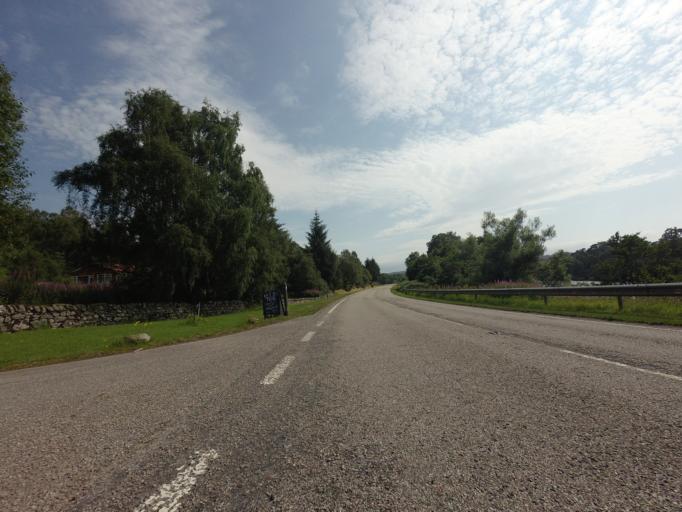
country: GB
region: Scotland
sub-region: Highland
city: Evanton
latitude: 57.9235
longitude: -4.3993
